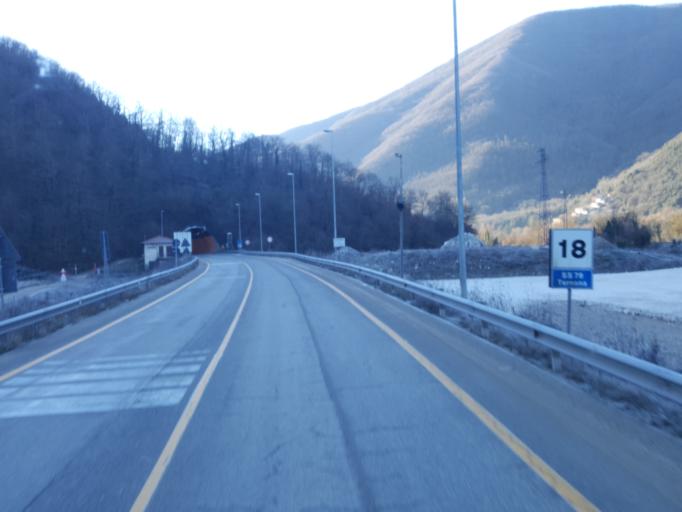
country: IT
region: Latium
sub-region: Provincia di Rieti
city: Colli sul Velino
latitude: 42.5046
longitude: 12.7466
